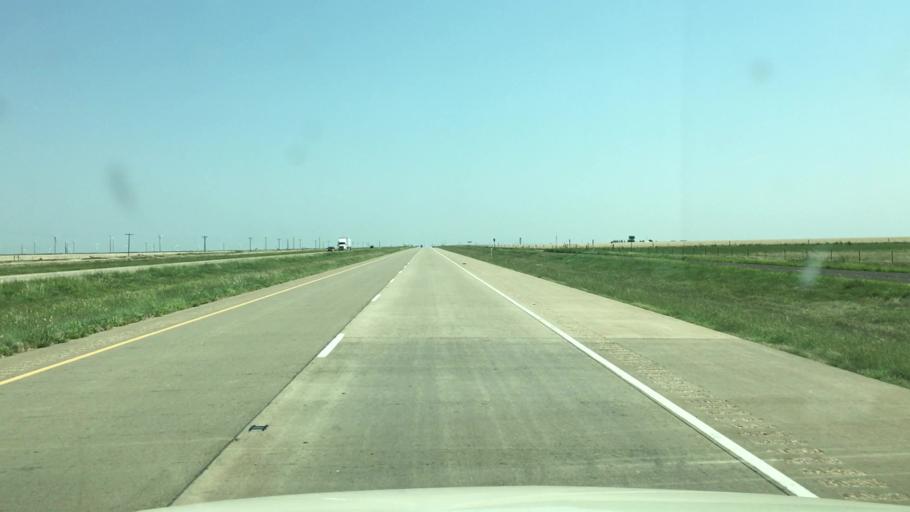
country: US
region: Texas
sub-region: Oldham County
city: Vega
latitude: 35.2727
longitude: -102.6133
